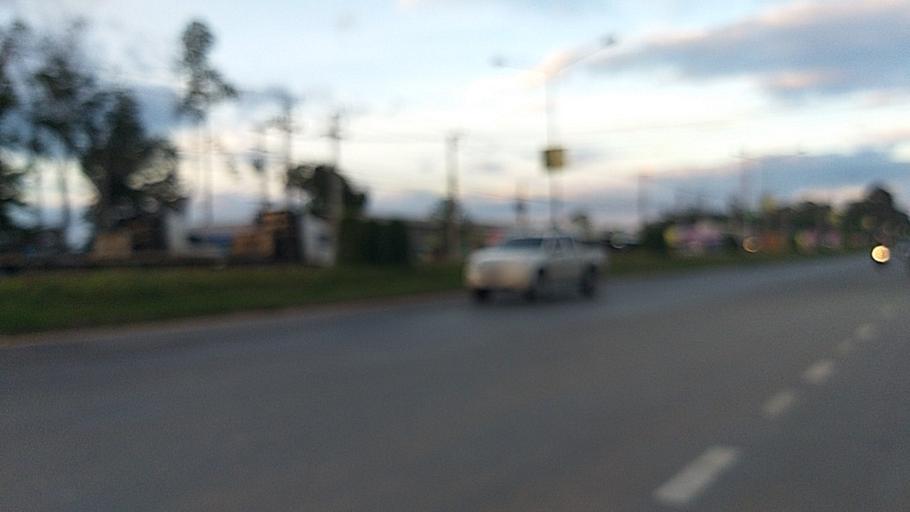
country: TH
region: Surin
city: Kap Choeng
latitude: 14.4528
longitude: 103.6916
